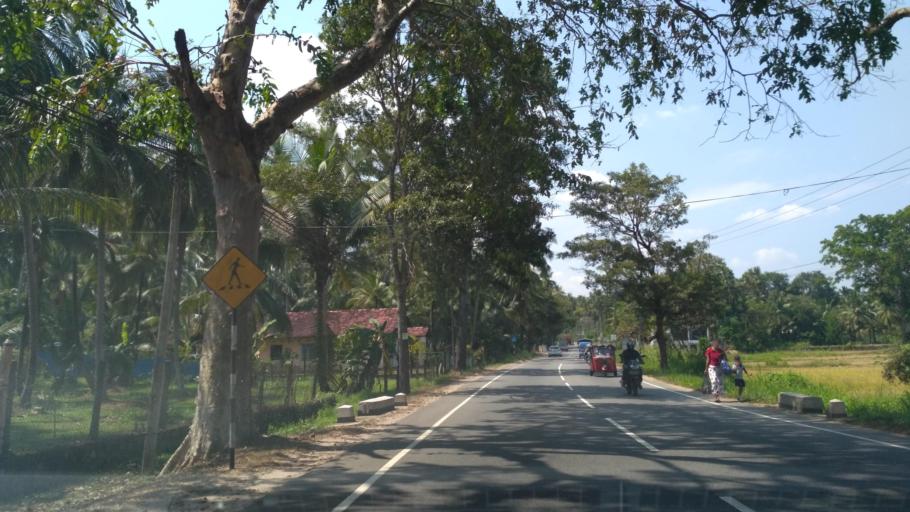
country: LK
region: North Western
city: Kurunegala
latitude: 7.4528
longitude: 80.2784
